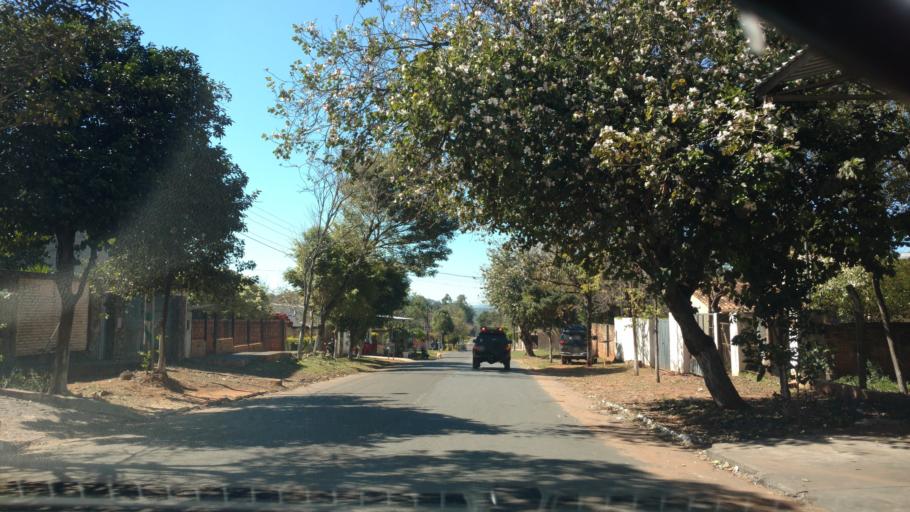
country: PY
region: Paraguari
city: Yaguaron
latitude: -25.5597
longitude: -57.2902
